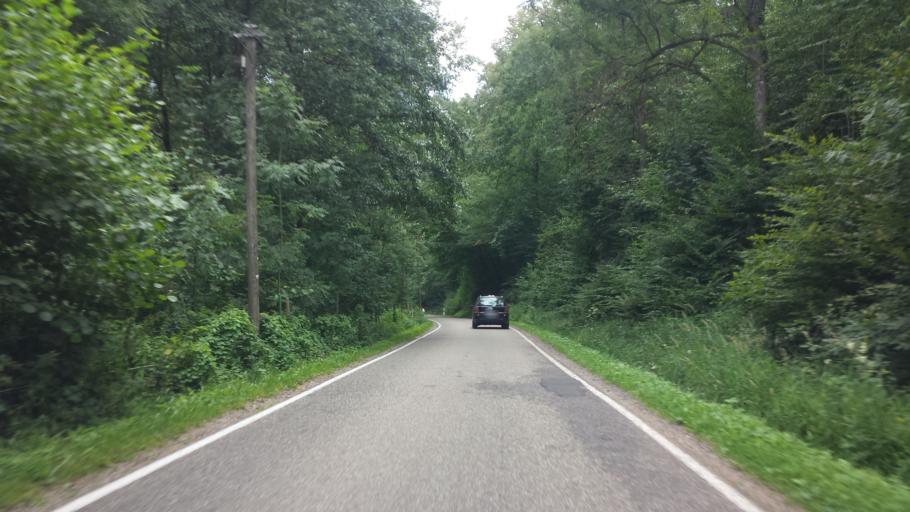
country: DE
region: Rheinland-Pfalz
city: Gleisweiler
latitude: 49.2702
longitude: 8.0470
